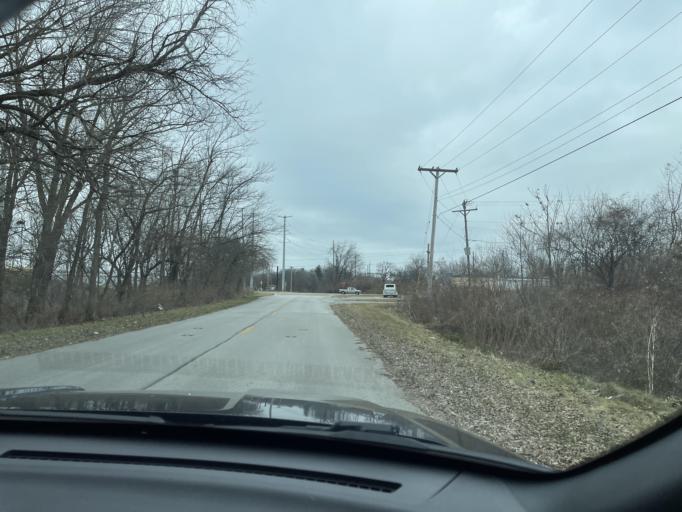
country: US
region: Illinois
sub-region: Sangamon County
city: Grandview
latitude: 39.7988
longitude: -89.6043
